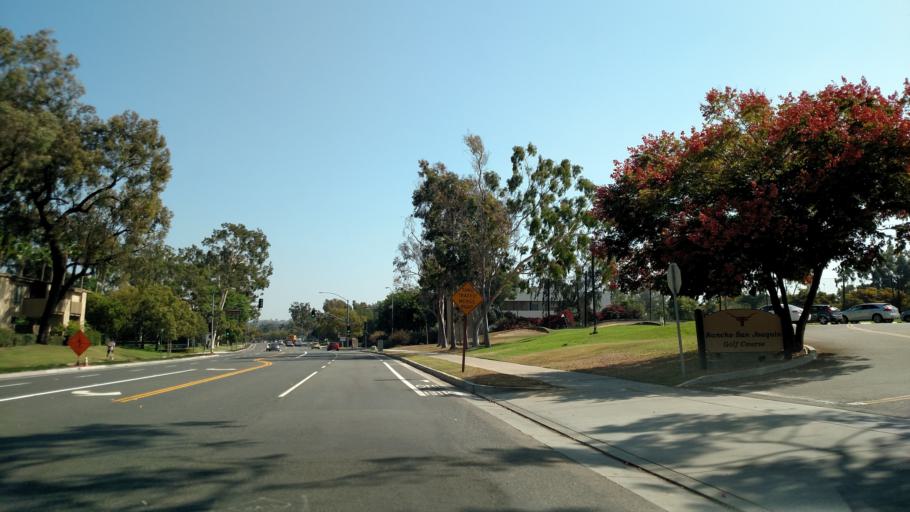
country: US
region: California
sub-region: Orange County
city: Irvine
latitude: 33.6679
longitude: -117.8294
